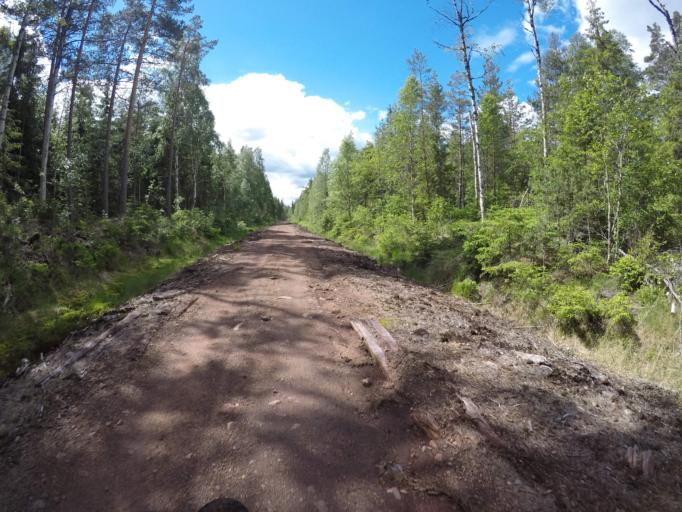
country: SE
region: Vaermland
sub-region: Filipstads Kommun
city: Lesjofors
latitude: 60.1361
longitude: 14.3378
